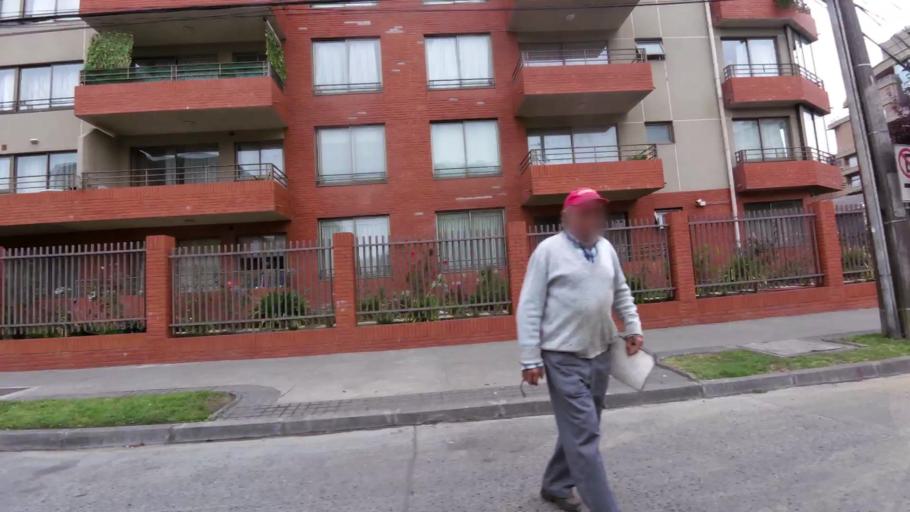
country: CL
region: Biobio
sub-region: Provincia de Concepcion
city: Concepcion
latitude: -36.8207
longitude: -73.0354
